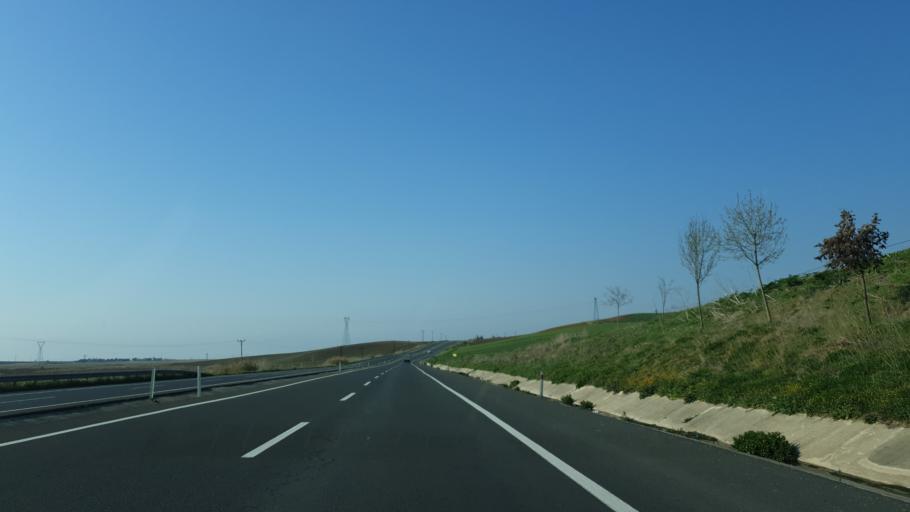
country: TR
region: Tekirdag
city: Corlu
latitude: 41.0378
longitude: 27.7301
